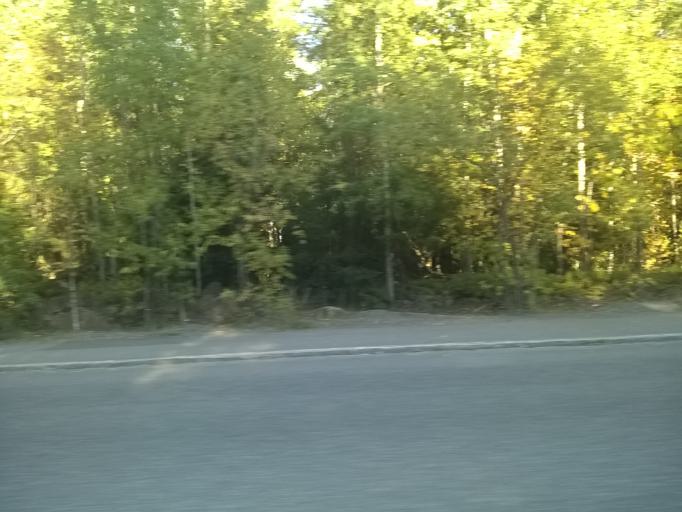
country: FI
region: Pirkanmaa
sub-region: Tampere
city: Tampere
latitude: 61.4549
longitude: 23.8355
